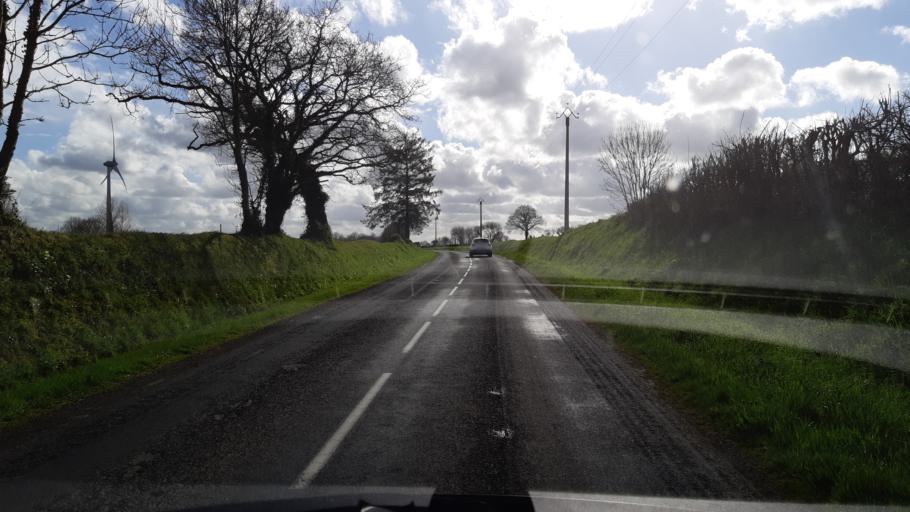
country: FR
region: Lower Normandy
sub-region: Departement de la Manche
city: Agneaux
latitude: 49.0236
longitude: -1.1572
